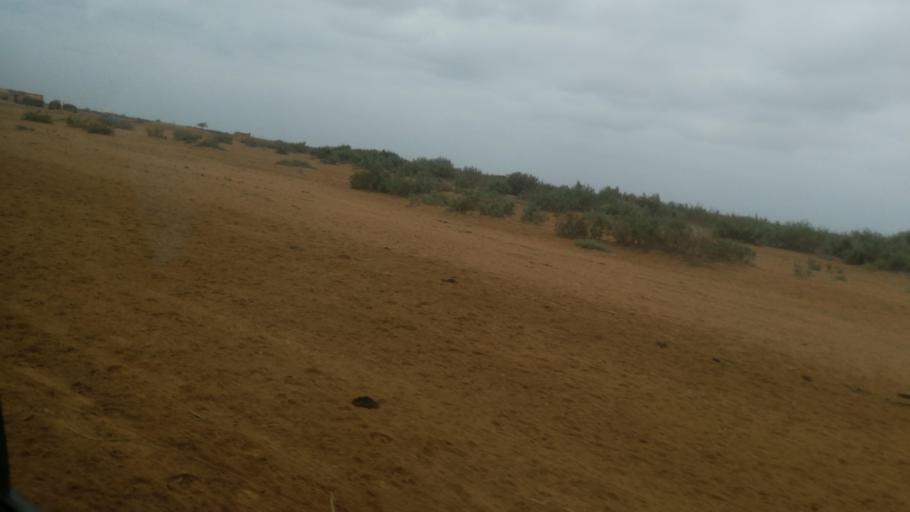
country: SN
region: Saint-Louis
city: Saint-Louis
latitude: 16.3145
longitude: -16.2293
